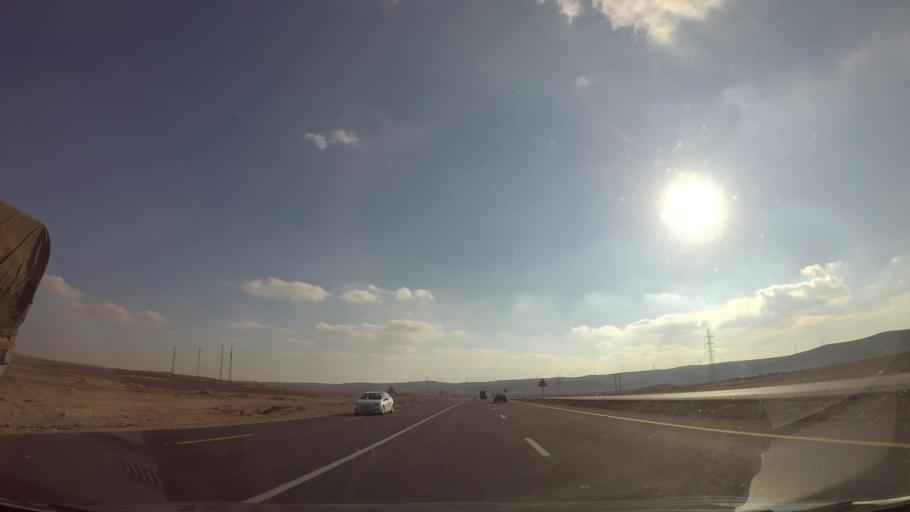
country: JO
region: Karak
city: Karak City
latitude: 31.1170
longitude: 36.0095
